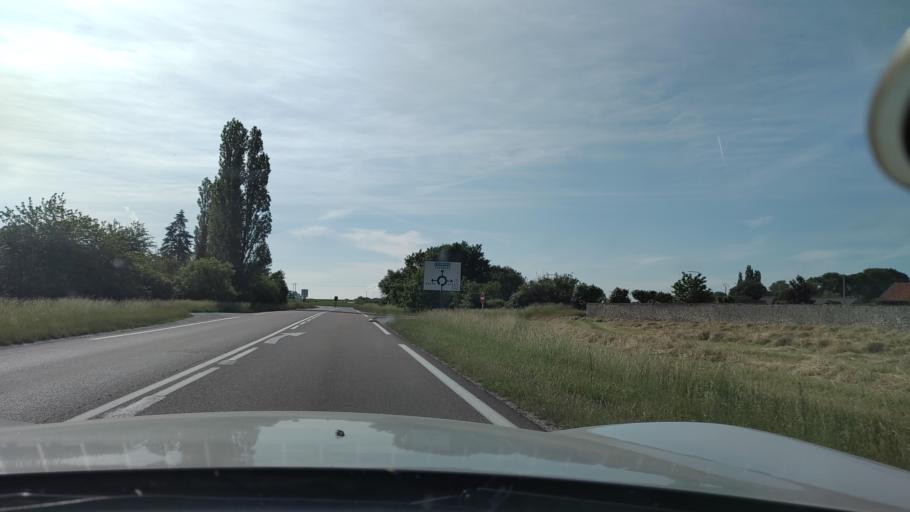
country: FR
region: Ile-de-France
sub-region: Departement de Seine-et-Marne
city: Jouy-le-Chatel
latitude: 48.6703
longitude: 3.1282
